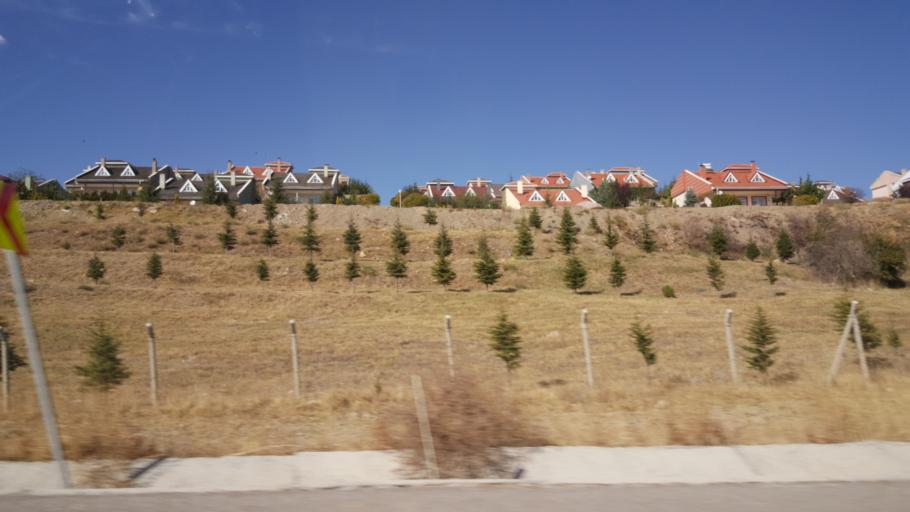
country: TR
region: Ankara
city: Ikizce
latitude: 39.5440
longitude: 32.6454
